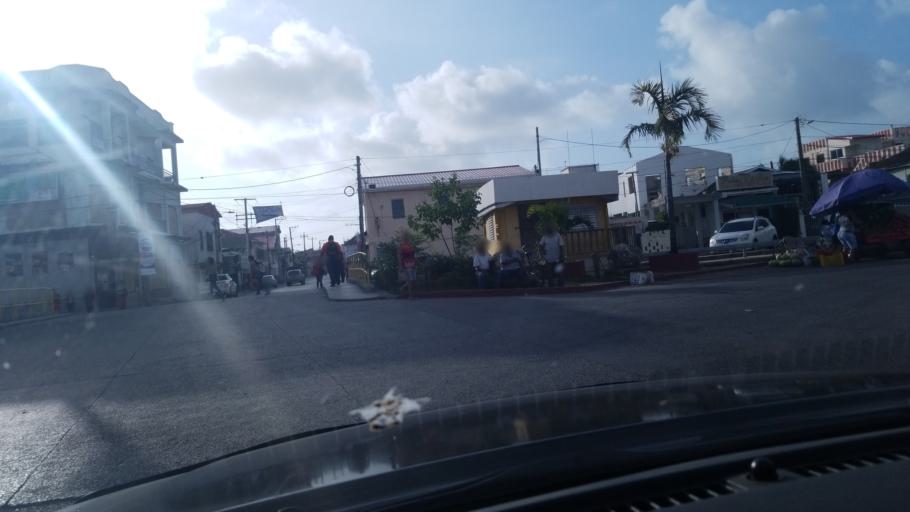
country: BZ
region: Belize
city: Belize City
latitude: 17.4953
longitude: -88.1927
